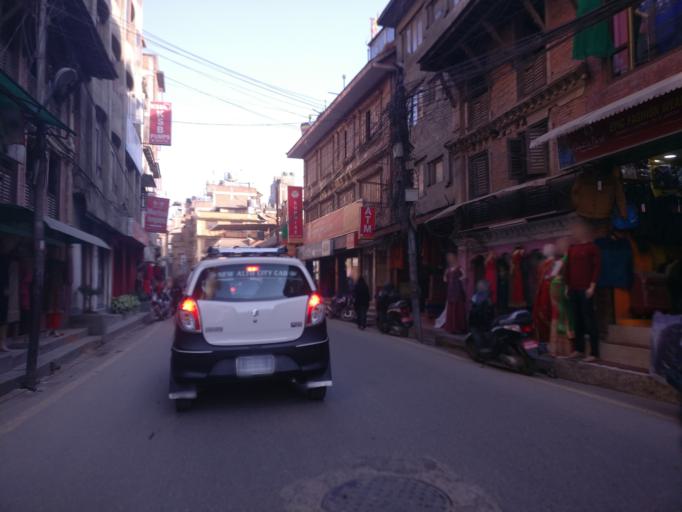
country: NP
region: Central Region
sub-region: Bagmati Zone
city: Patan
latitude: 27.6741
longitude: 85.3214
